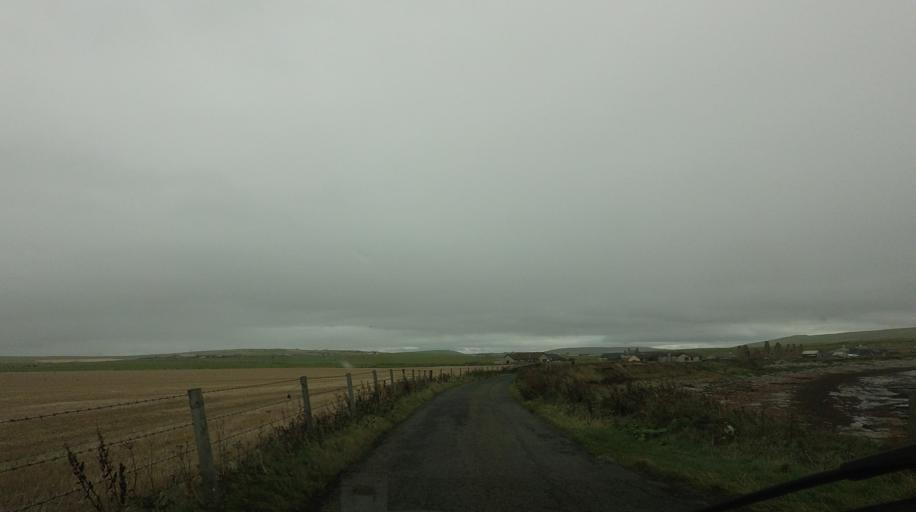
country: GB
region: Scotland
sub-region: Orkney Islands
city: Stromness
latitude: 59.1334
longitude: -3.3194
